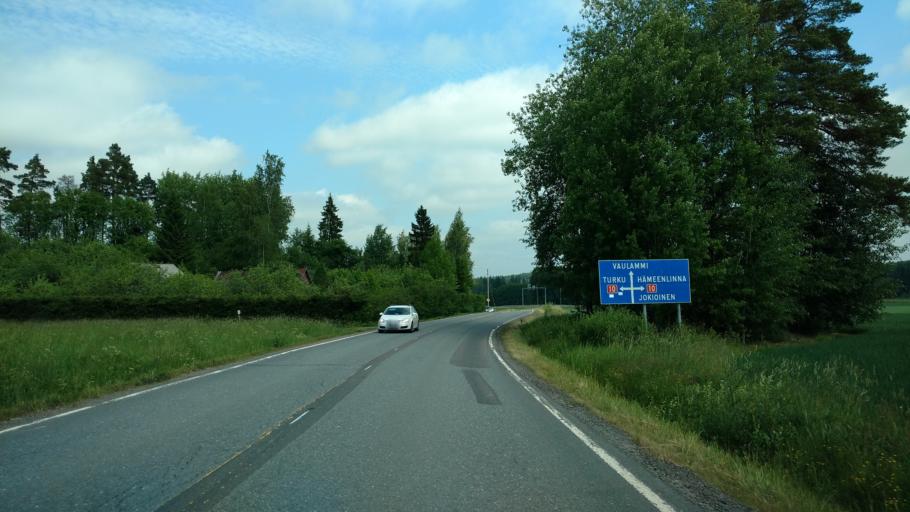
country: FI
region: Haeme
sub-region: Forssa
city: Jokioinen
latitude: 60.7783
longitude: 23.4206
